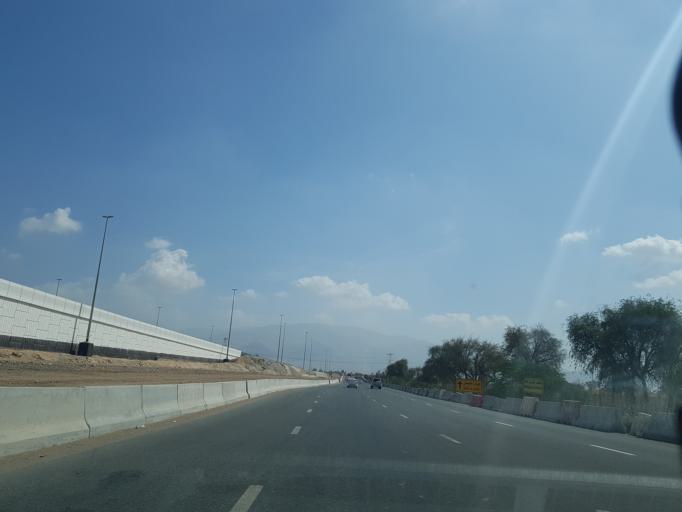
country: AE
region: Ra's al Khaymah
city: Ras al-Khaimah
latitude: 25.6989
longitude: 55.9691
